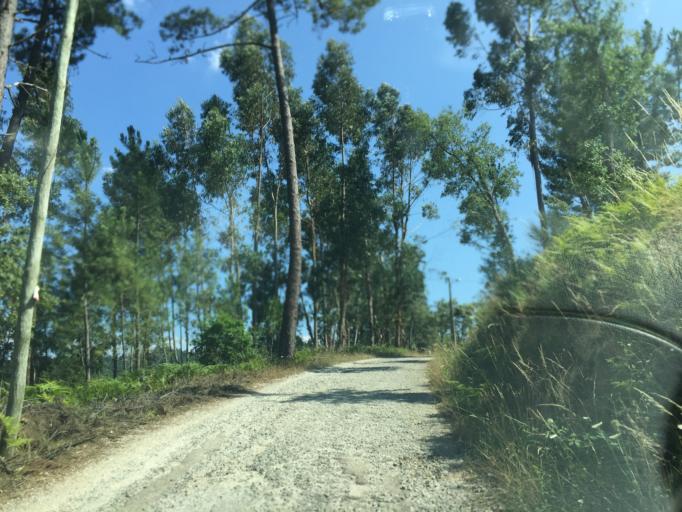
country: PT
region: Leiria
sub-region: Pedrogao Grande
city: Pedrogao Grande
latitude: 39.9257
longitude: -8.1333
